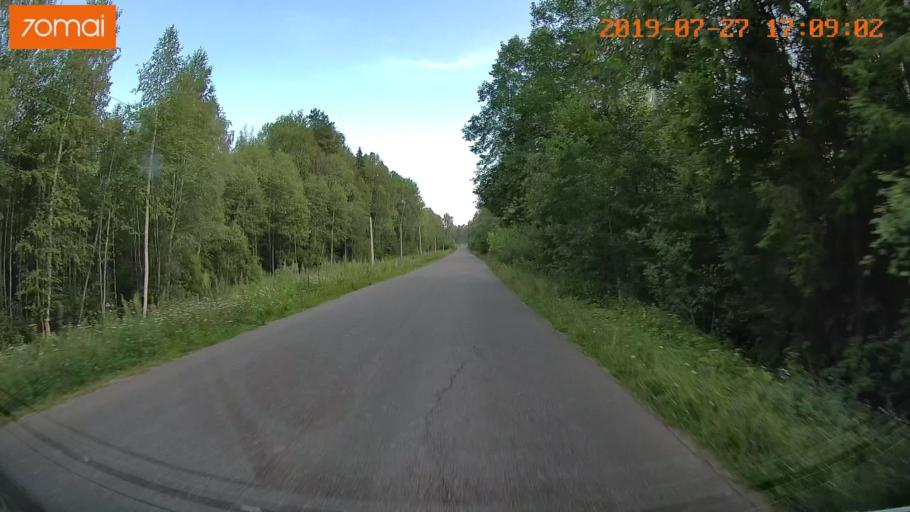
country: RU
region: Ivanovo
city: Novo-Talitsy
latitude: 57.0773
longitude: 40.8449
